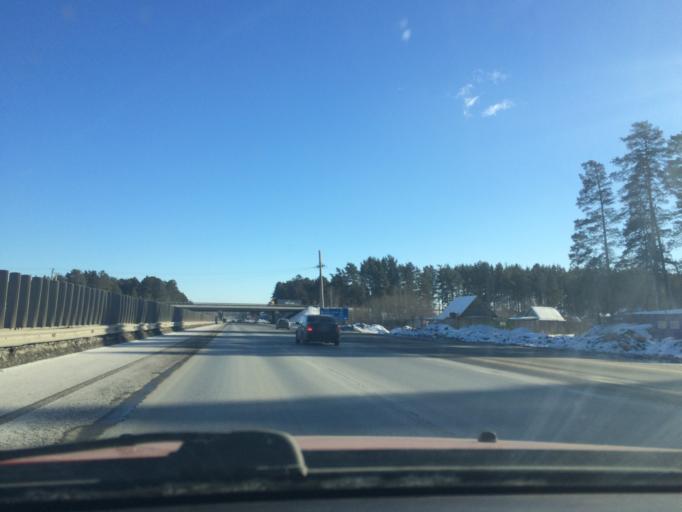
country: RU
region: Sverdlovsk
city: Istok
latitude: 56.8042
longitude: 60.7864
